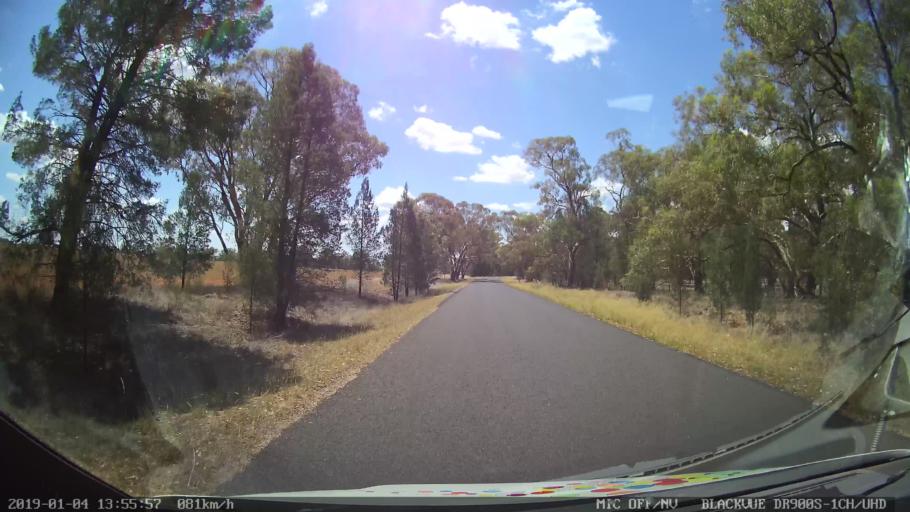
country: AU
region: New South Wales
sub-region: Dubbo Municipality
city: Dubbo
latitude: -32.3564
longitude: 148.5908
